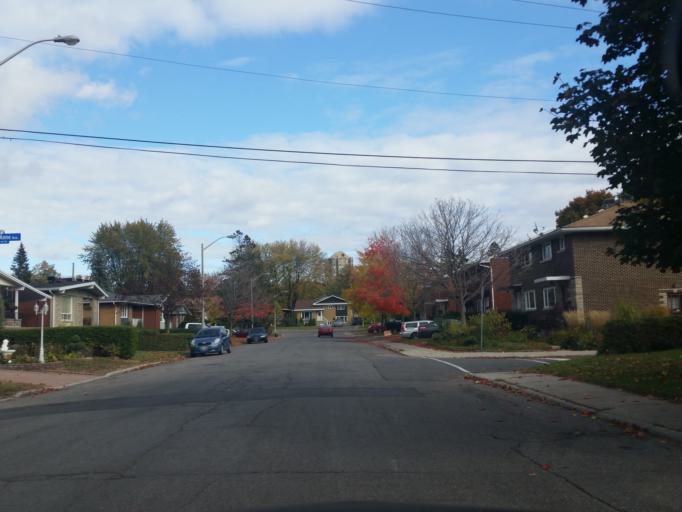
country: CA
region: Ontario
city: Ottawa
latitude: 45.4422
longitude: -75.6598
